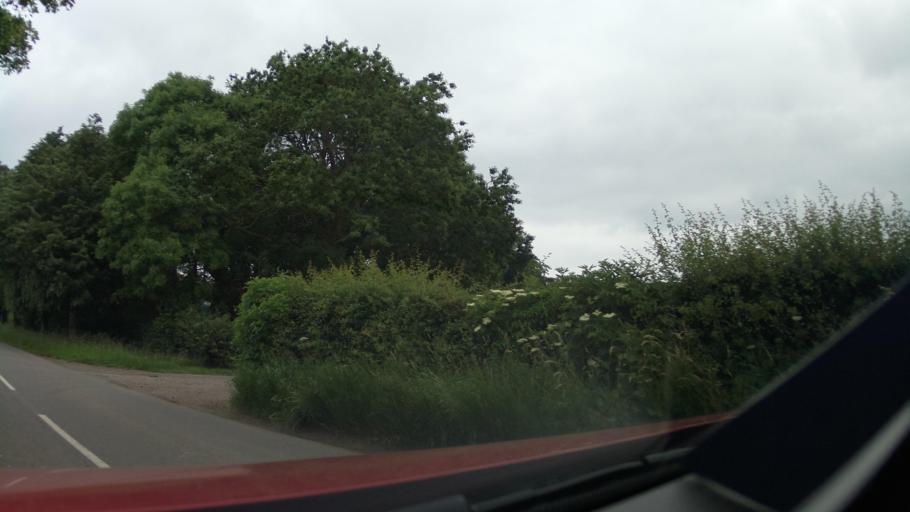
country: GB
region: England
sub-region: Leicestershire
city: Melton Mowbray
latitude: 52.6917
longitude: -0.8433
